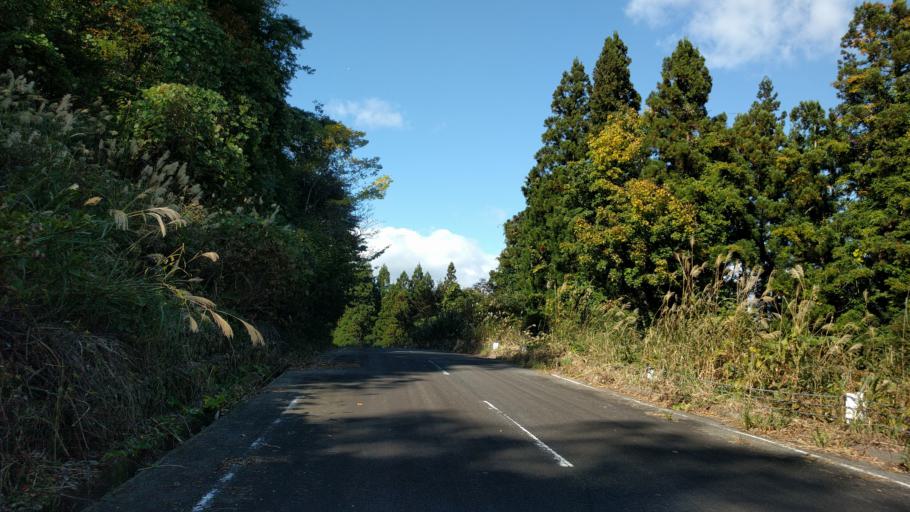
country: JP
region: Fukushima
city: Kitakata
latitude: 37.4360
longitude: 139.7803
